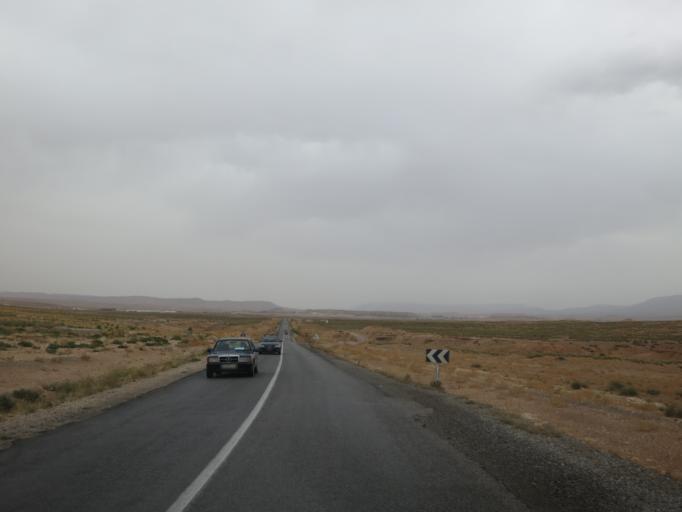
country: MA
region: Meknes-Tafilalet
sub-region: Khenifra
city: Midelt
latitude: 32.6976
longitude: -4.8418
